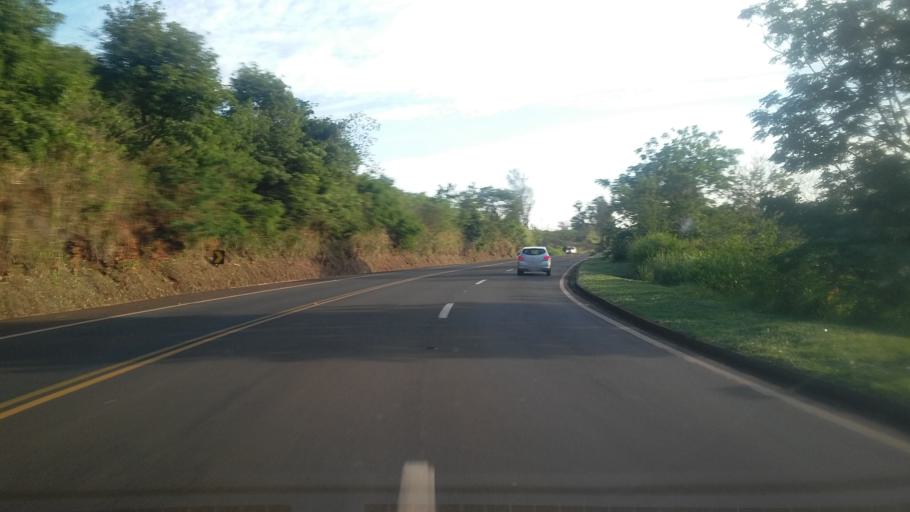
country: BR
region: Parana
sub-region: Assai
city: Assai
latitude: -23.2291
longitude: -50.6780
